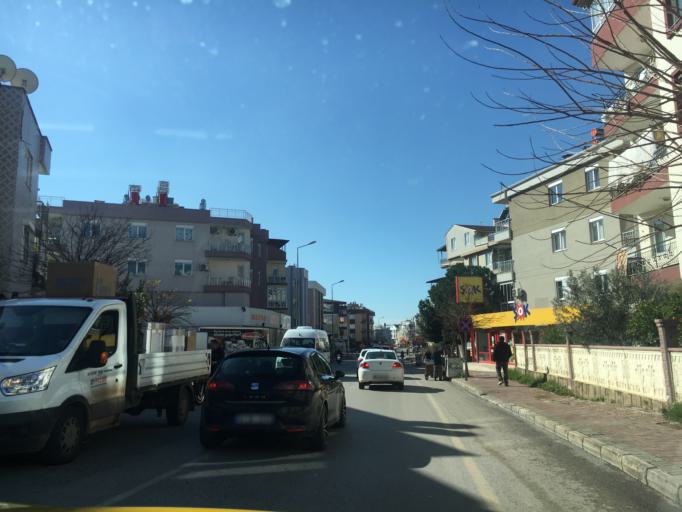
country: TR
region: Antalya
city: Antalya
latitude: 36.9163
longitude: 30.7068
